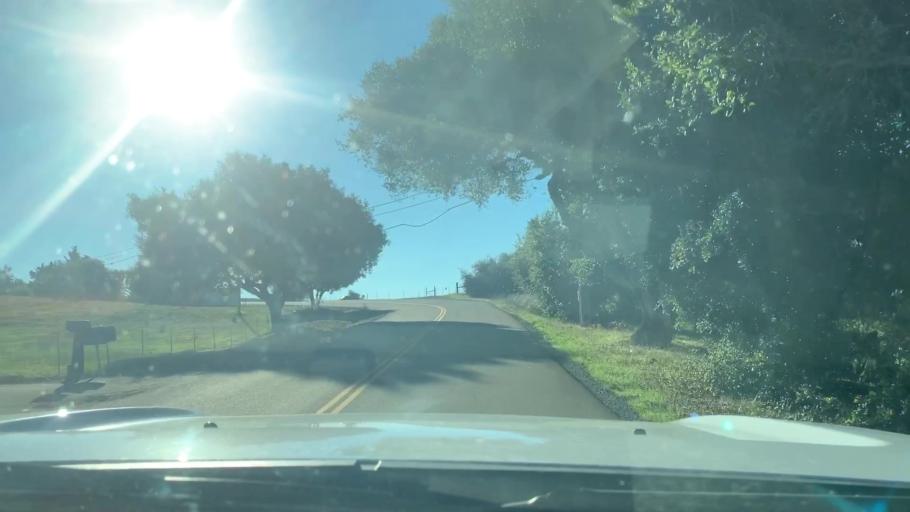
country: US
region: California
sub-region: San Luis Obispo County
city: Arroyo Grande
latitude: 35.1066
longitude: -120.5615
